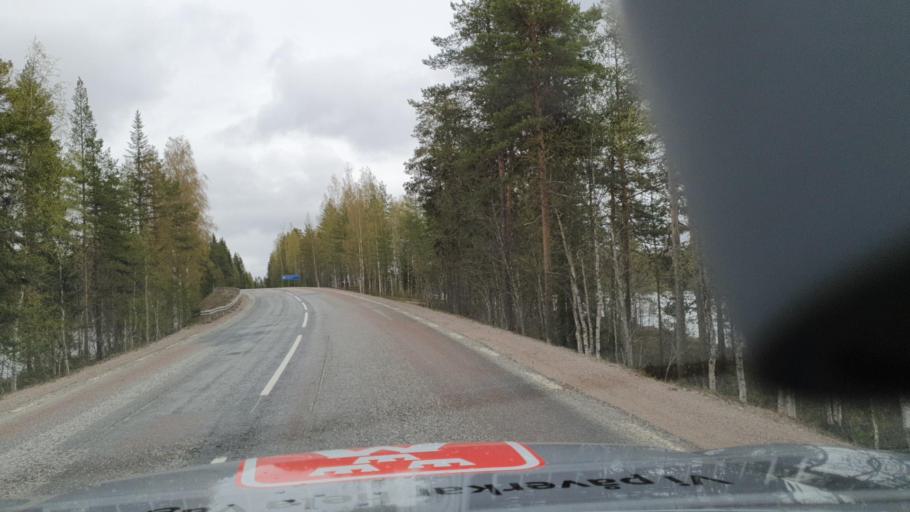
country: SE
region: Vaesternorrland
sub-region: Solleftea Kommun
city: Solleftea
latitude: 63.6544
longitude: 17.2802
